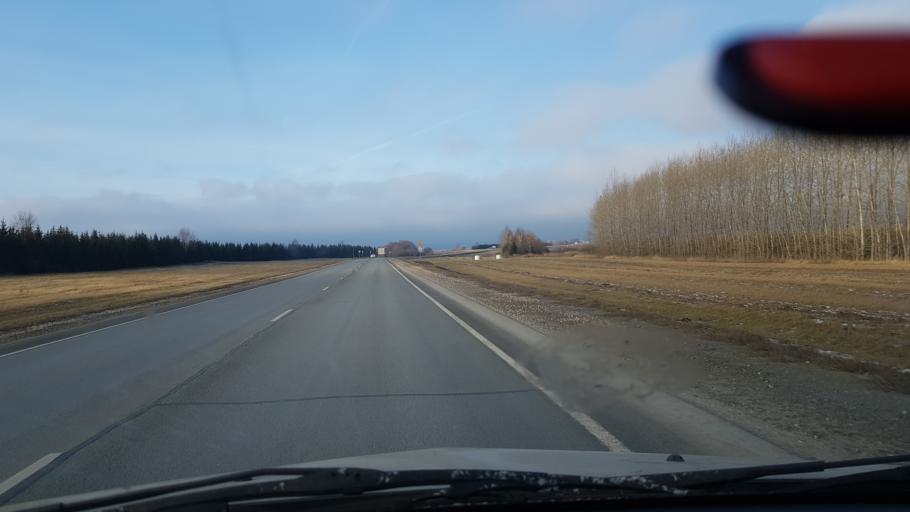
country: RU
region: Tatarstan
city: Laishevo
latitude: 55.3969
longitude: 49.7735
